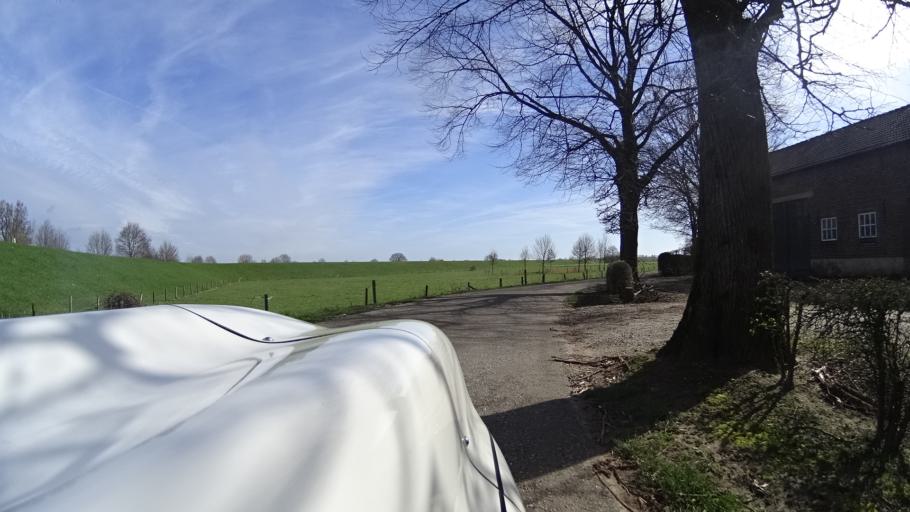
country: NL
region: Limburg
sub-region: Gemeente Gennep
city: Gennep
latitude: 51.7096
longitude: 5.9280
